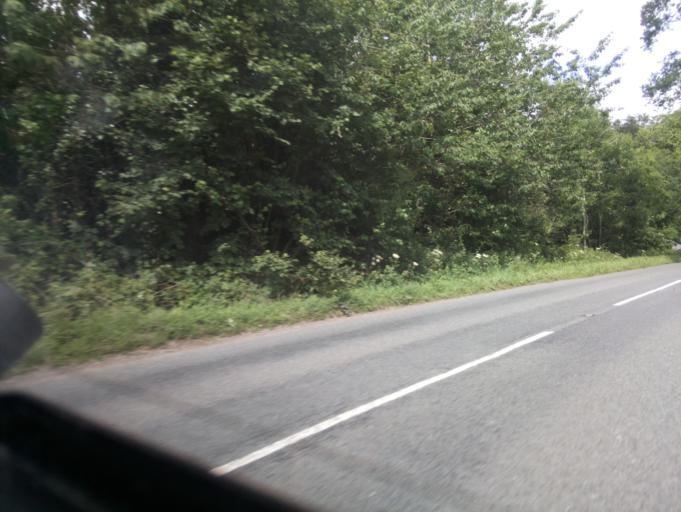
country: GB
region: England
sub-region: Gloucestershire
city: Lydney
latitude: 51.7347
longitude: -2.5490
